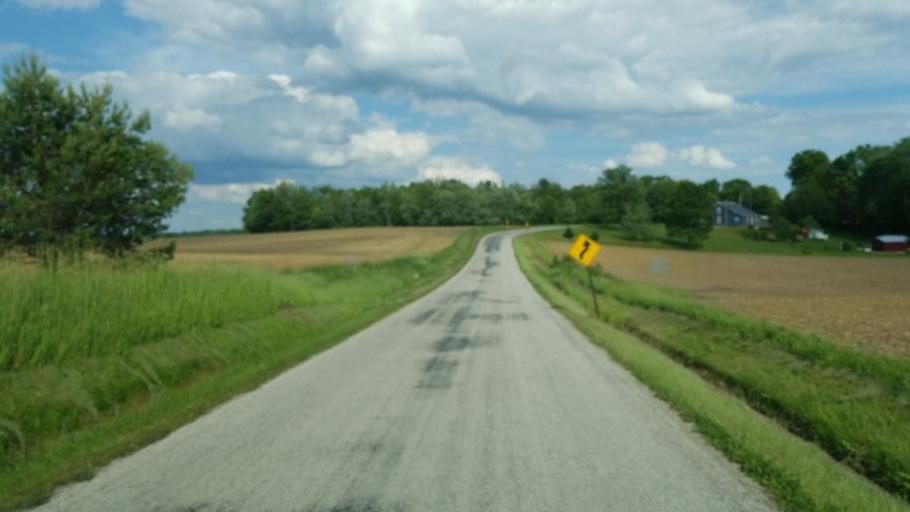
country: US
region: Ohio
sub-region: Richland County
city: Lincoln Heights
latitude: 40.8670
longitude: -82.5103
